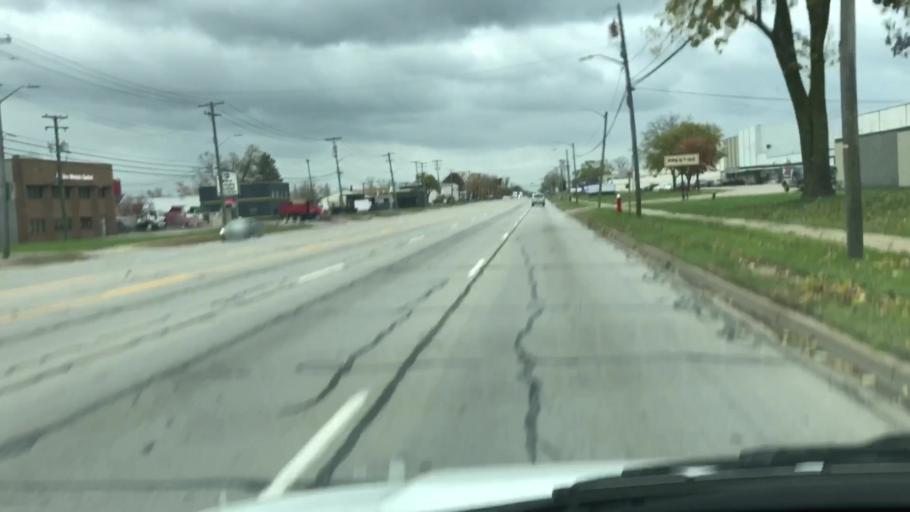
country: US
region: Michigan
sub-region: Macomb County
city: Eastpointe
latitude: 42.4893
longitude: -82.9727
